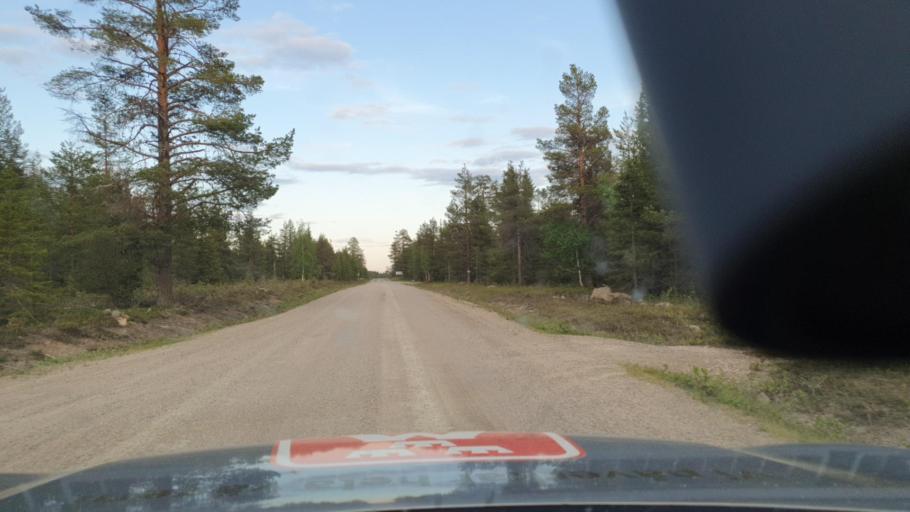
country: SE
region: Norrbotten
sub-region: Bodens Kommun
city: Boden
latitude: 66.5568
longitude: 21.4444
